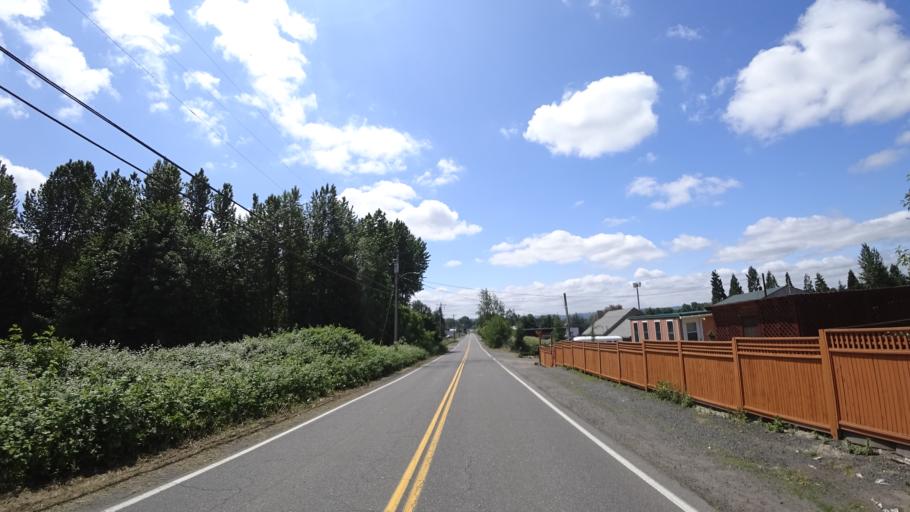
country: US
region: Washington
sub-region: Clark County
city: Vancouver
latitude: 45.5975
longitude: -122.6610
